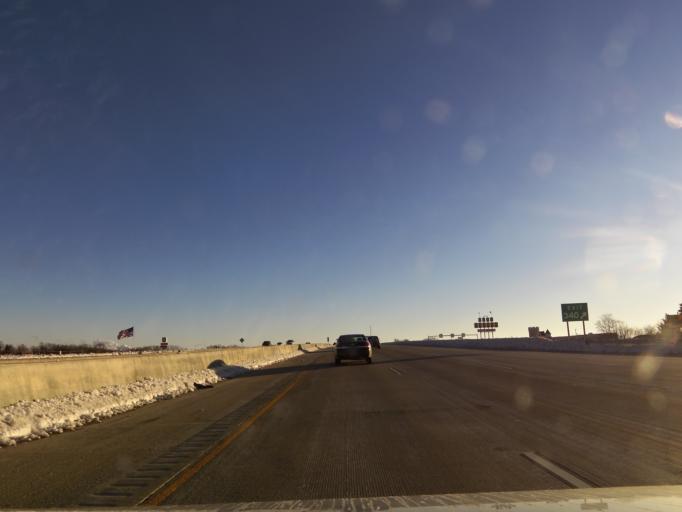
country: US
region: Wisconsin
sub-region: Kenosha County
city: Somers
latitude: 42.6181
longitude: -87.9524
